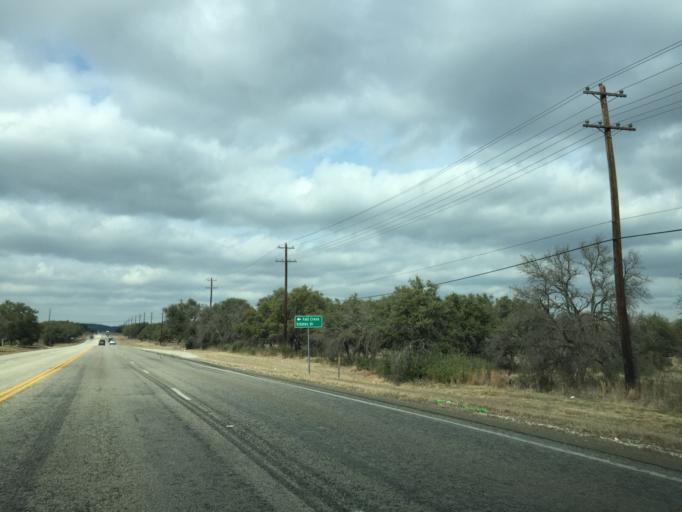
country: US
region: Texas
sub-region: Travis County
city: Briarcliff
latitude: 30.4109
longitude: -98.1109
